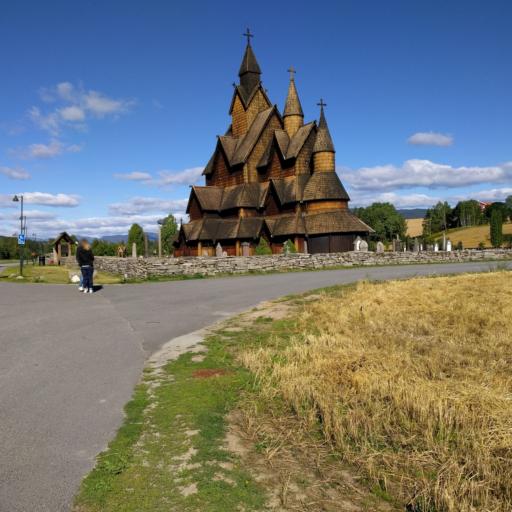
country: NO
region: Telemark
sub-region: Notodden
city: Notodden
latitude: 59.5793
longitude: 9.1771
